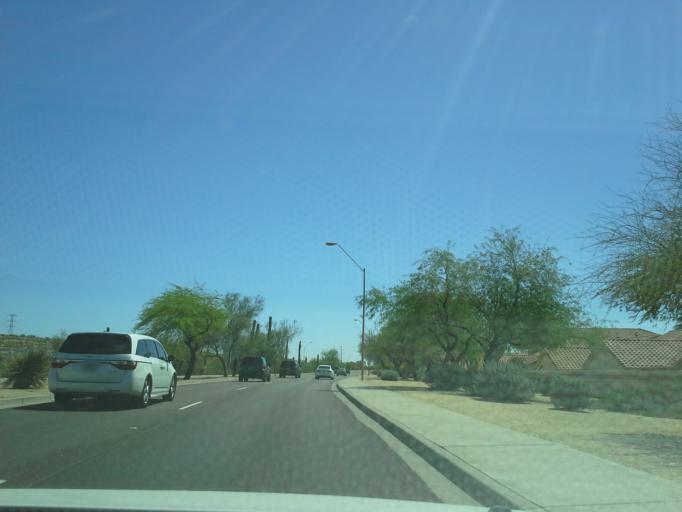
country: US
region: Arizona
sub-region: Maricopa County
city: Scottsdale
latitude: 33.6101
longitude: -111.8585
